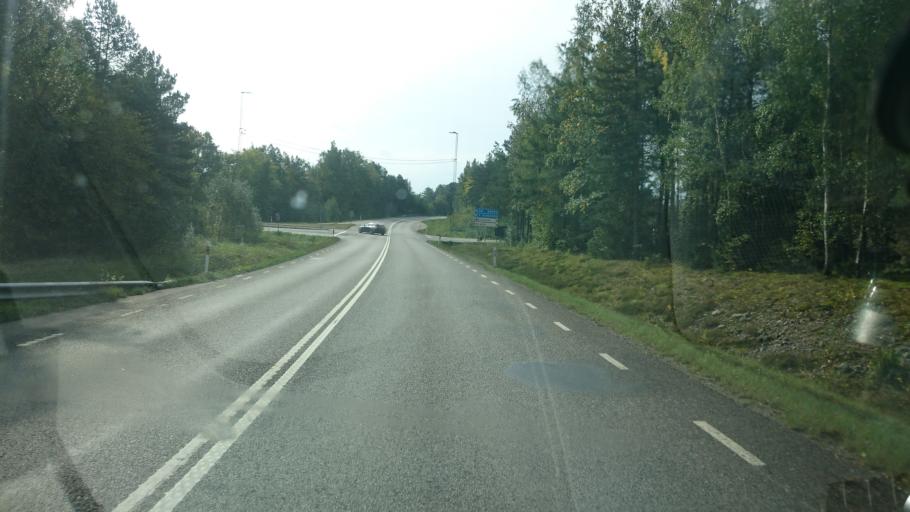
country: SE
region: Vaestra Goetaland
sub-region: Alingsas Kommun
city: Alingsas
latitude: 57.9765
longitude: 12.4334
